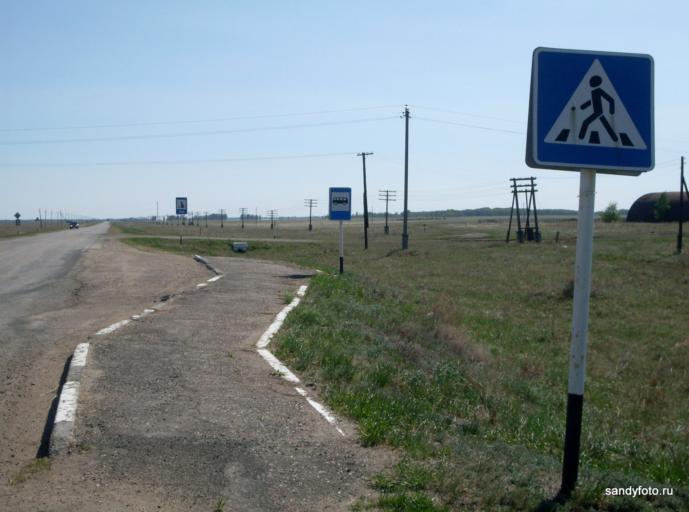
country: RU
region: Chelyabinsk
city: Bobrovka
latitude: 54.1647
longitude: 61.8248
